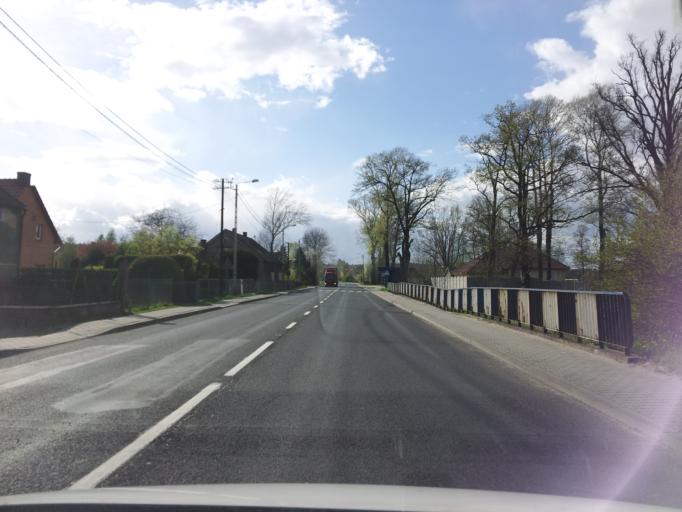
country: PL
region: Lubusz
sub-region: Powiat krosnienski
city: Dabie
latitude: 51.9874
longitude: 15.2644
